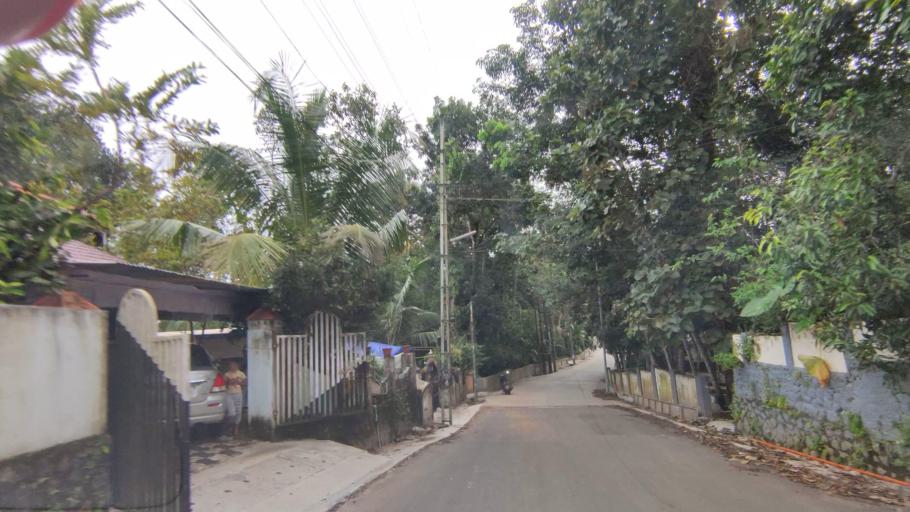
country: IN
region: Kerala
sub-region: Kottayam
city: Kottayam
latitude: 9.6631
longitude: 76.5168
